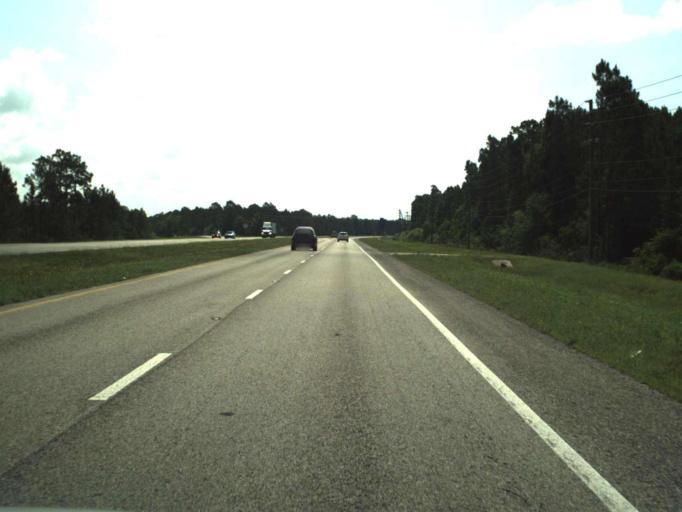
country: US
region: Florida
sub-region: Volusia County
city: Samsula-Spruce Creek
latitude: 29.0250
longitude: -81.1290
